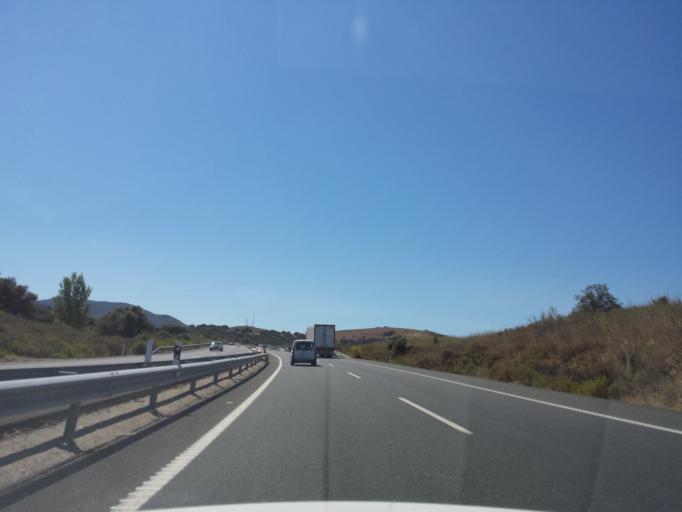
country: ES
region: Extremadura
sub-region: Provincia de Caceres
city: Casas de Miravete
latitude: 39.7693
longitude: -5.7367
